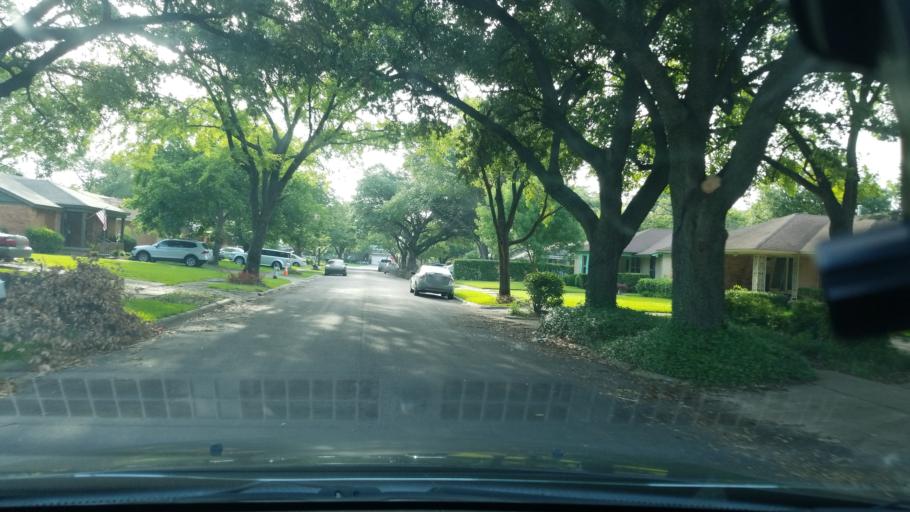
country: US
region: Texas
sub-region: Dallas County
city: Garland
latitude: 32.8313
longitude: -96.6624
